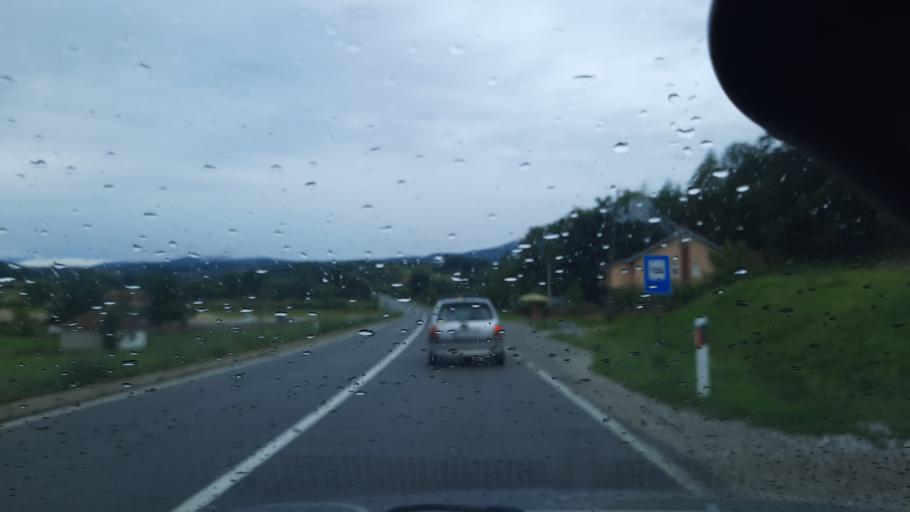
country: RS
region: Central Serbia
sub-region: Sumadijski Okrug
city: Knic
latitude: 43.8569
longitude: 20.7754
